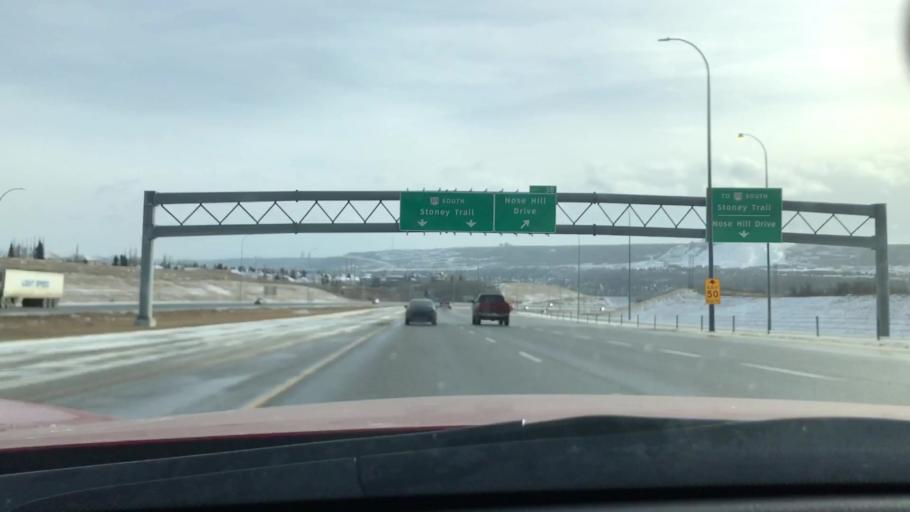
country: CA
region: Alberta
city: Calgary
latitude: 51.1136
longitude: -114.2273
